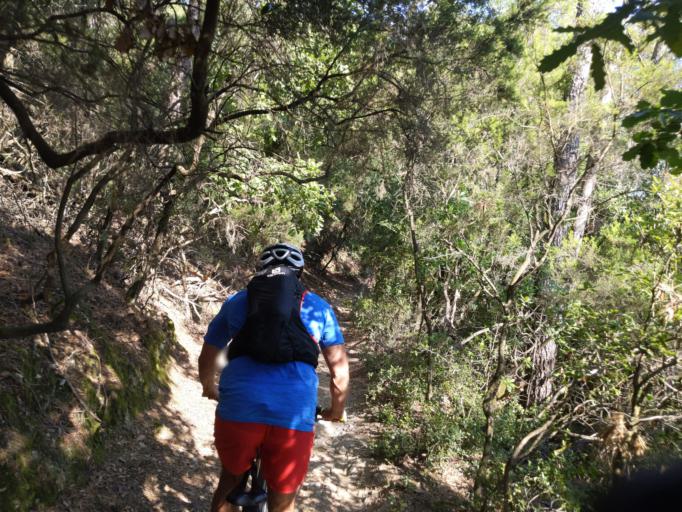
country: ES
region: Catalonia
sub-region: Provincia de Barcelona
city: Cerdanyola del Valles
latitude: 41.4652
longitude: 2.1334
